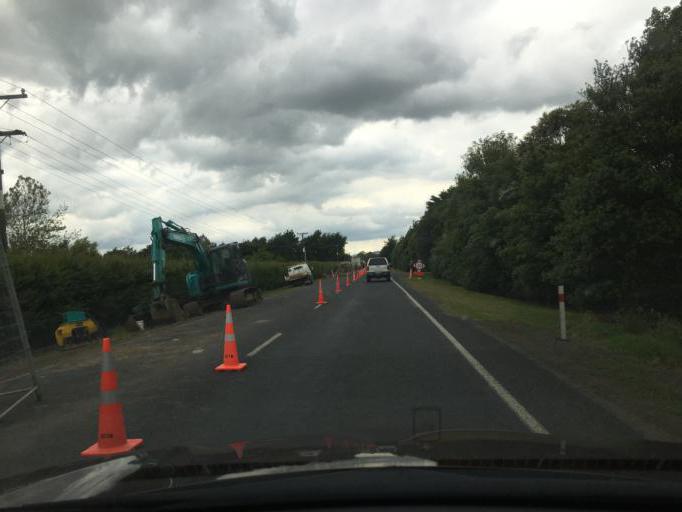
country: NZ
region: Waikato
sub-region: Waipa District
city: Cambridge
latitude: -37.9177
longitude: 175.4418
